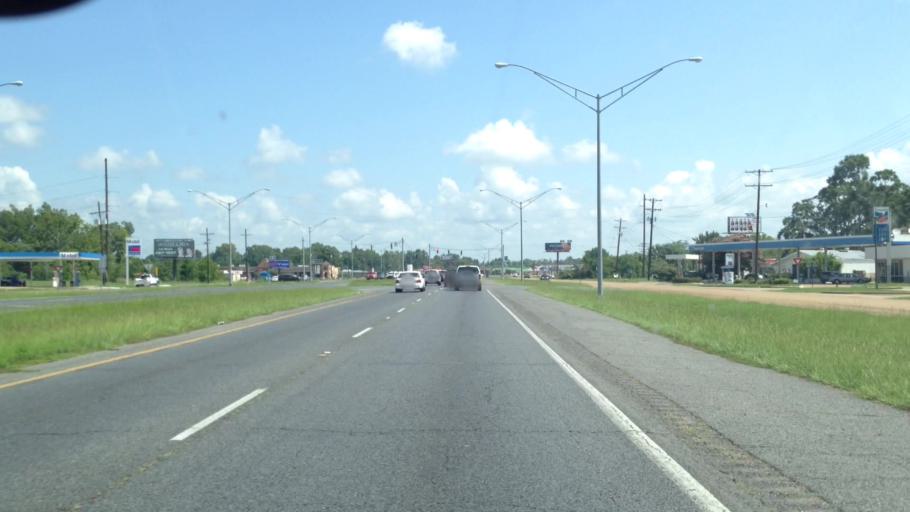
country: US
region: Louisiana
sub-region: Rapides Parish
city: Alexandria
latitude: 31.3032
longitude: -92.4799
